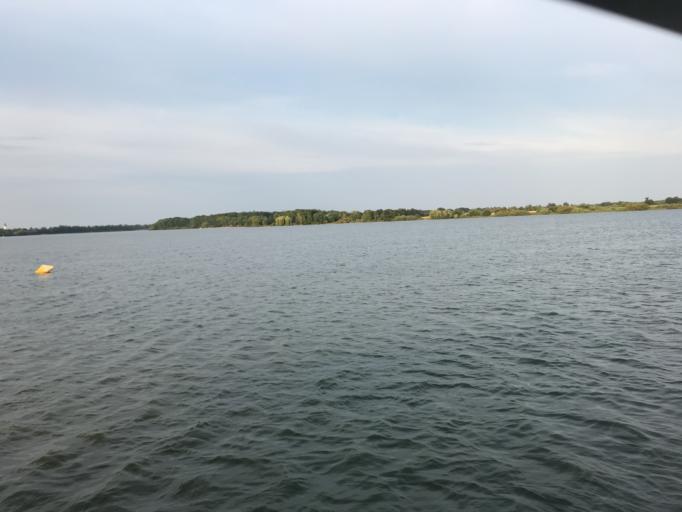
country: CZ
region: Jihocesky
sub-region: Okres Jindrichuv Hradec
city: Trebon
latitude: 48.9908
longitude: 14.7414
